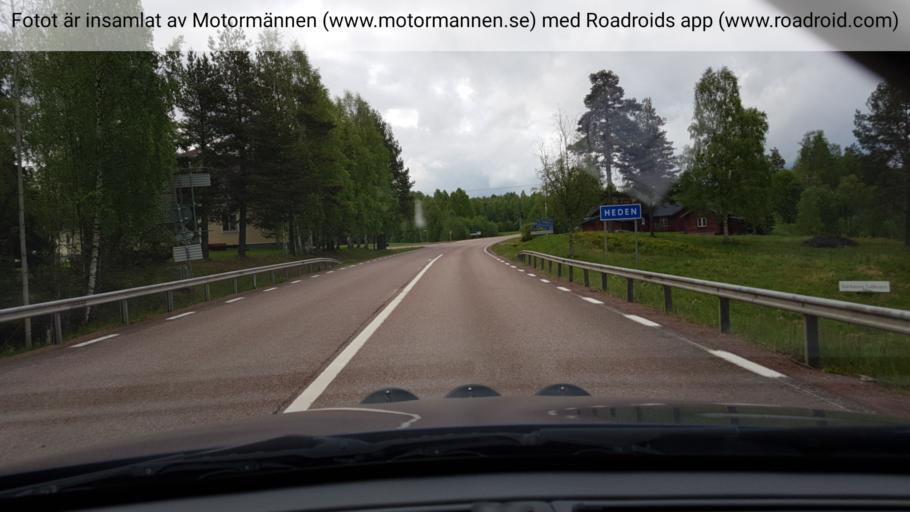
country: SE
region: Dalarna
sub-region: Orsa Kommun
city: Orsa
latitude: 61.1484
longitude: 14.6575
